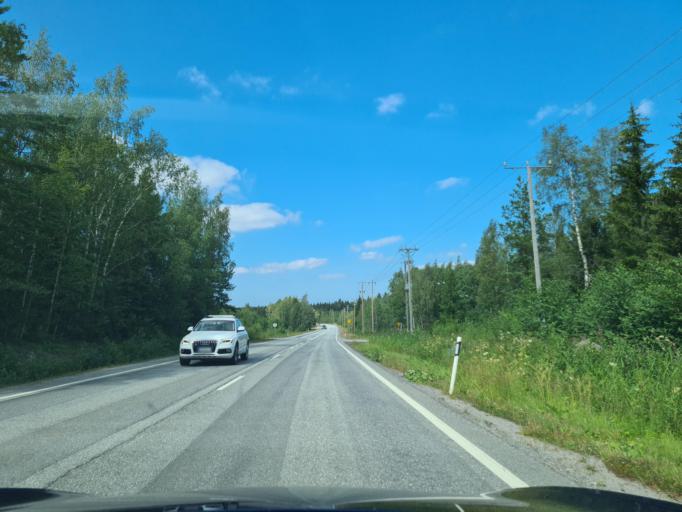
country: FI
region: Ostrobothnia
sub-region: Vaasa
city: Vaasa
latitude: 63.1860
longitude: 21.5666
